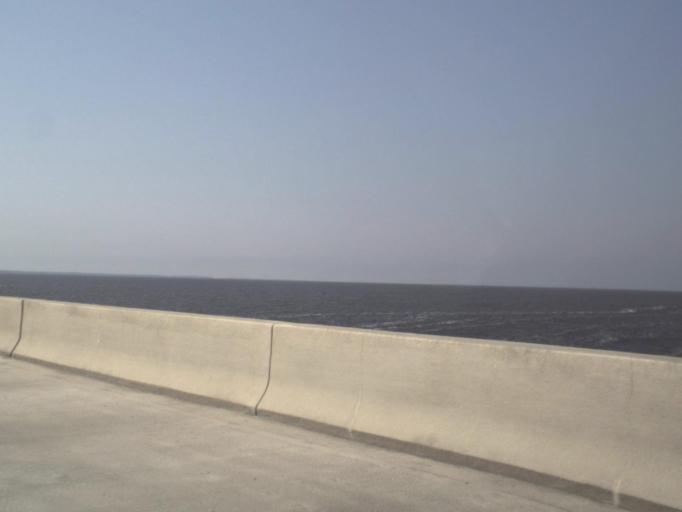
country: US
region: Florida
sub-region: Franklin County
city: Eastpoint
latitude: 29.7130
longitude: -84.8909
